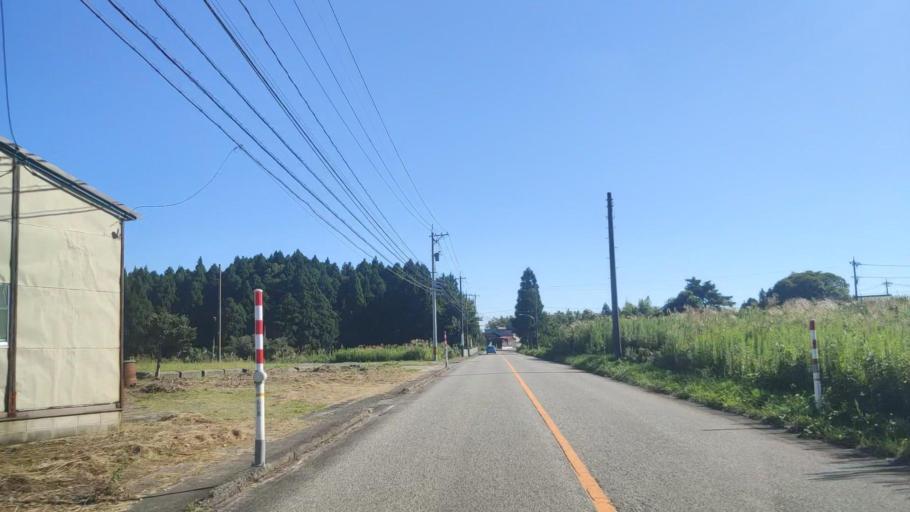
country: JP
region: Ishikawa
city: Nanao
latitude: 37.2595
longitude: 137.0891
